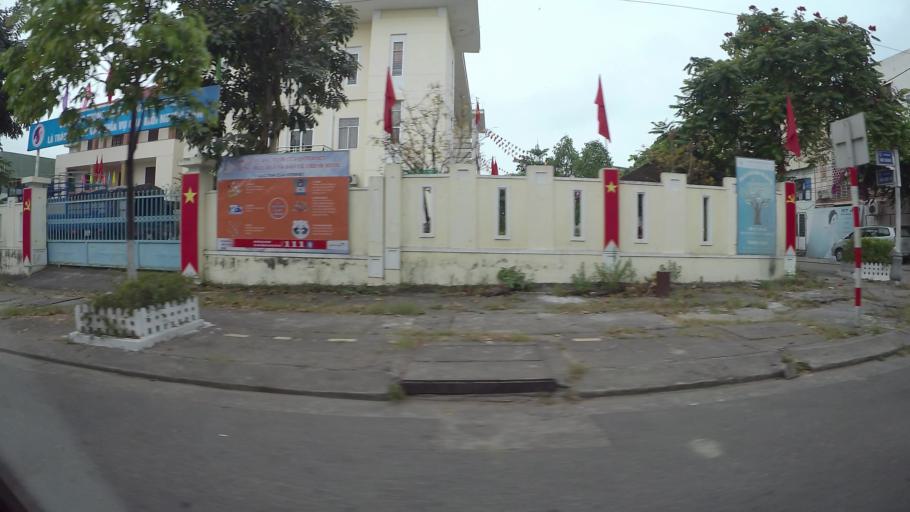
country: VN
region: Da Nang
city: Cam Le
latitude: 16.0280
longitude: 108.2219
